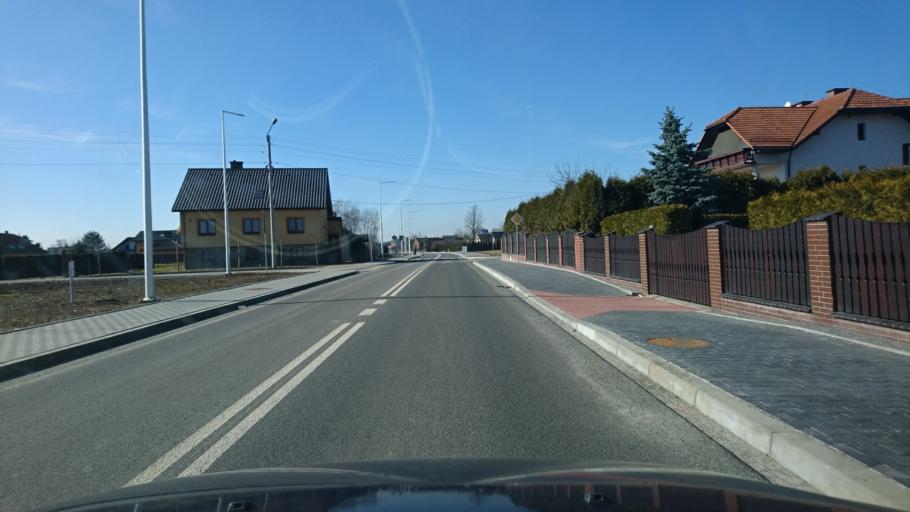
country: PL
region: Lesser Poland Voivodeship
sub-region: Powiat oswiecimski
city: Kety
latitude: 49.8918
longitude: 19.2161
